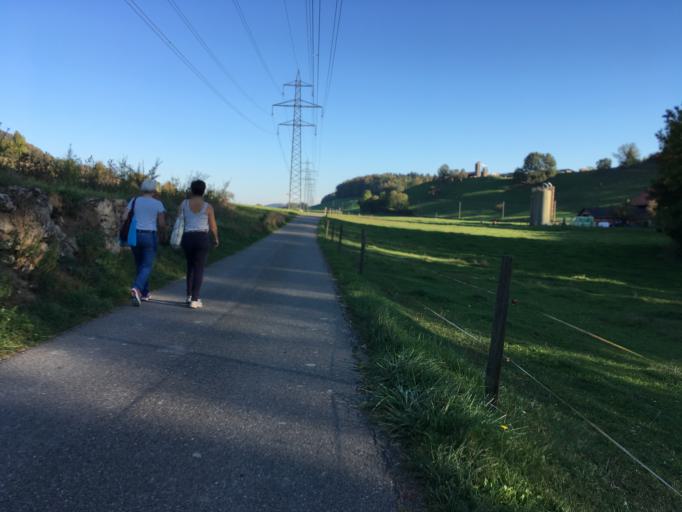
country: CH
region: Zurich
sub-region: Bezirk Buelach
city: Freienstein
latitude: 47.5352
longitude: 8.5888
